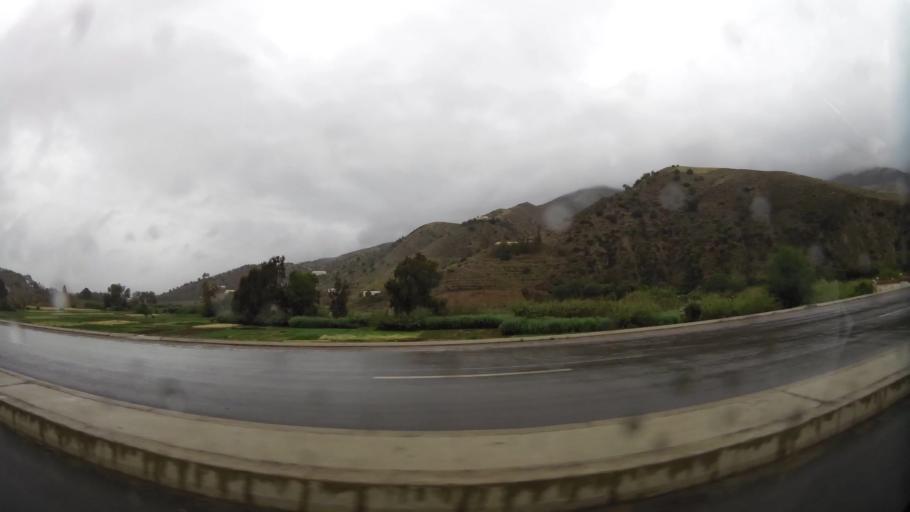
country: MA
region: Taza-Al Hoceima-Taounate
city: Imzourene
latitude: 35.0147
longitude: -3.8176
